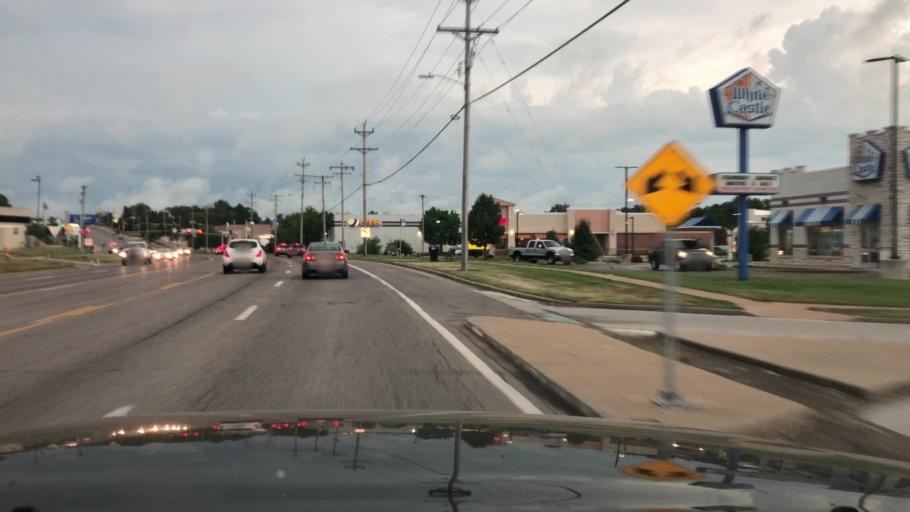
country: US
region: Missouri
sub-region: Saint Louis County
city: Bridgeton
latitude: 38.7478
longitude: -90.4227
